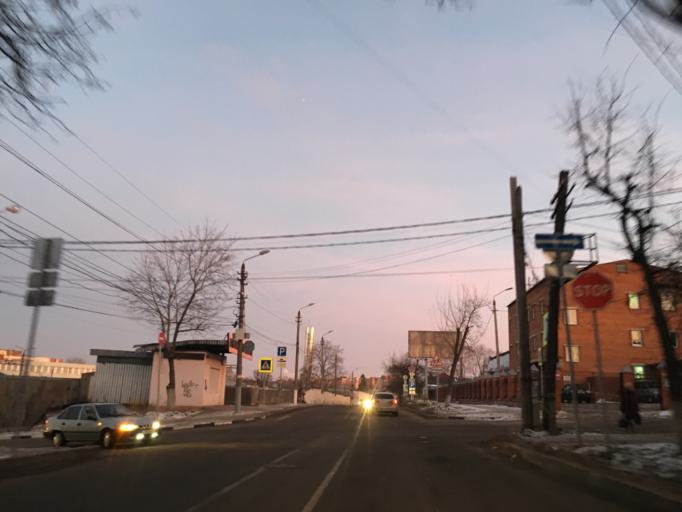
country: RU
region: Tula
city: Tula
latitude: 54.1854
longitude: 37.6165
